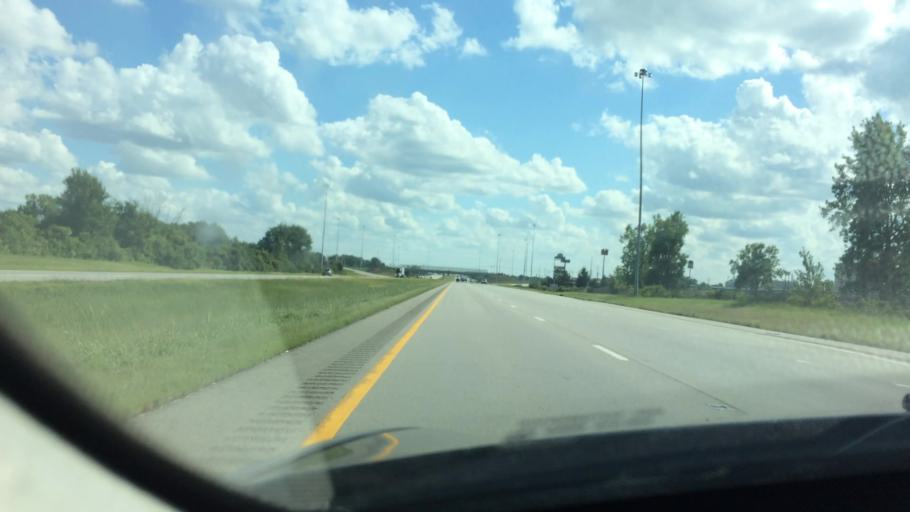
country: US
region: Ohio
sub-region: Shelby County
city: Sidney
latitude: 40.2938
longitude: -84.1819
